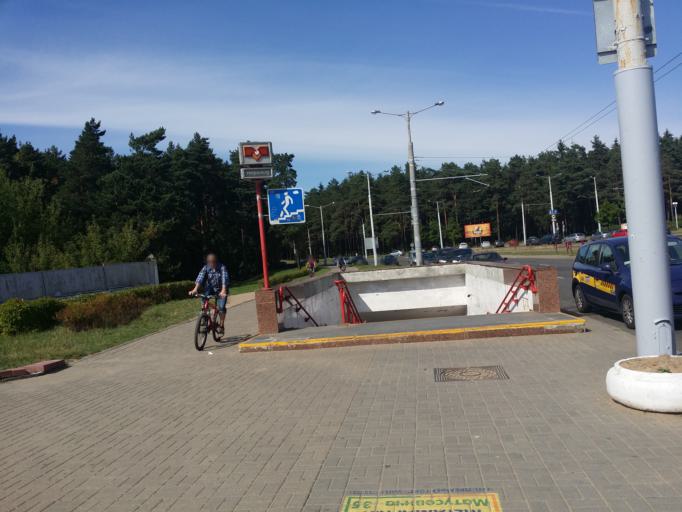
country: BY
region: Minsk
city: Minsk
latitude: 53.8767
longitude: 27.6268
